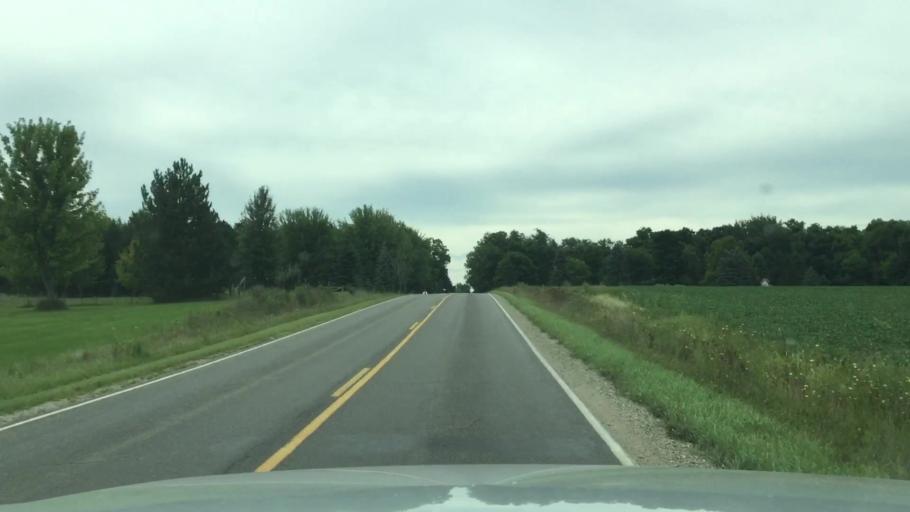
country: US
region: Michigan
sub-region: Shiawassee County
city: Durand
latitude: 42.9685
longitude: -83.9868
